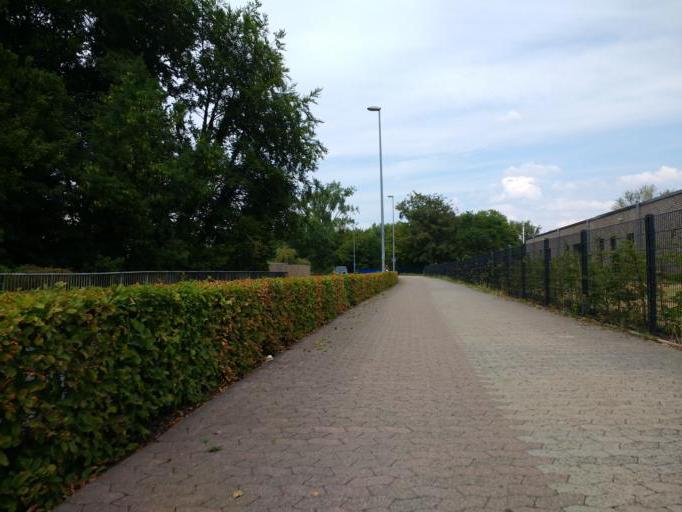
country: DE
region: Lower Saxony
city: Gifhorn
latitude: 52.4832
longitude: 10.5521
